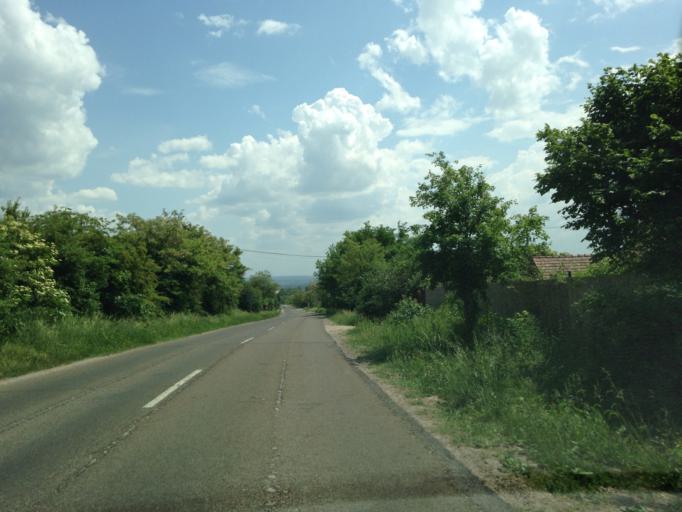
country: HU
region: Pest
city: Szentendre
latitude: 47.7002
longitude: 19.0341
